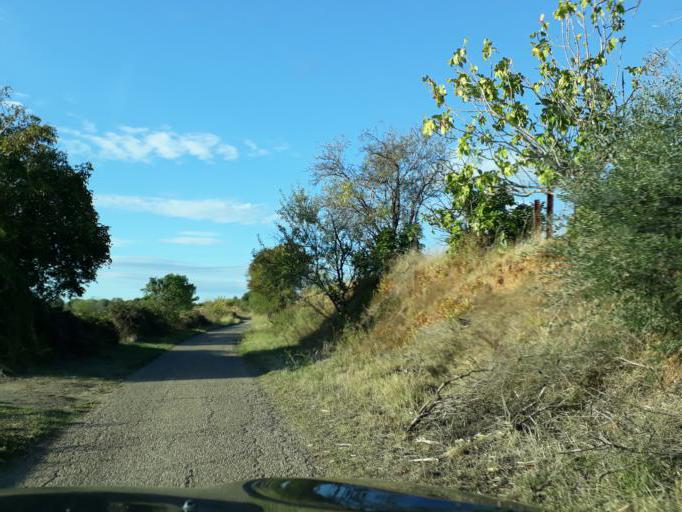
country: FR
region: Languedoc-Roussillon
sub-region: Departement de l'Herault
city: Florensac
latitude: 43.4118
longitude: 3.4753
